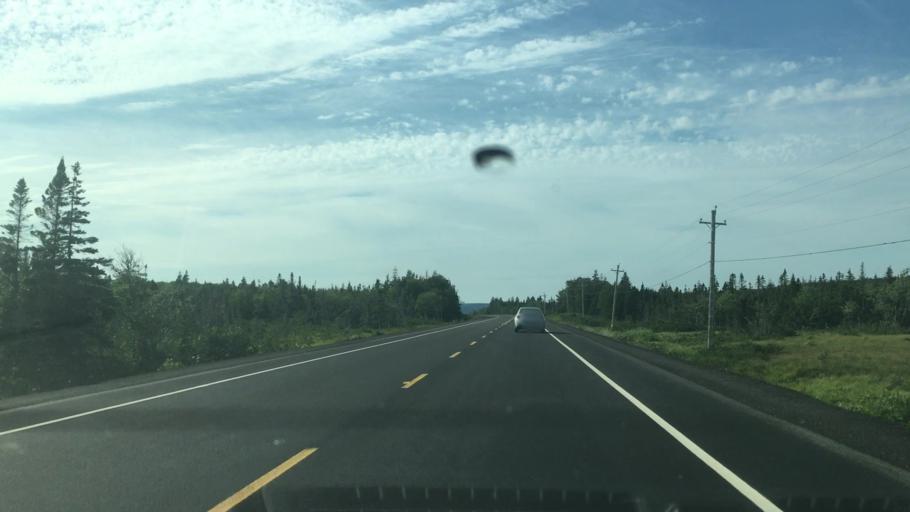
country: CA
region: Nova Scotia
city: Sydney Mines
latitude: 46.8475
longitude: -60.4139
